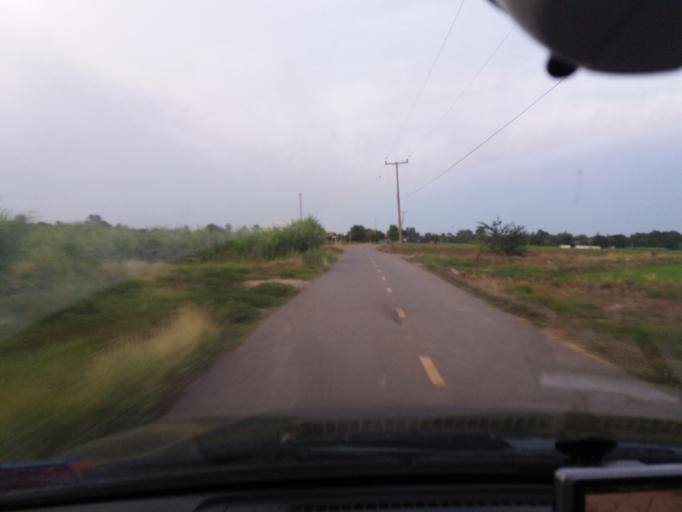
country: TH
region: Suphan Buri
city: Doembang Nangbuat
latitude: 14.8230
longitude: 100.1398
